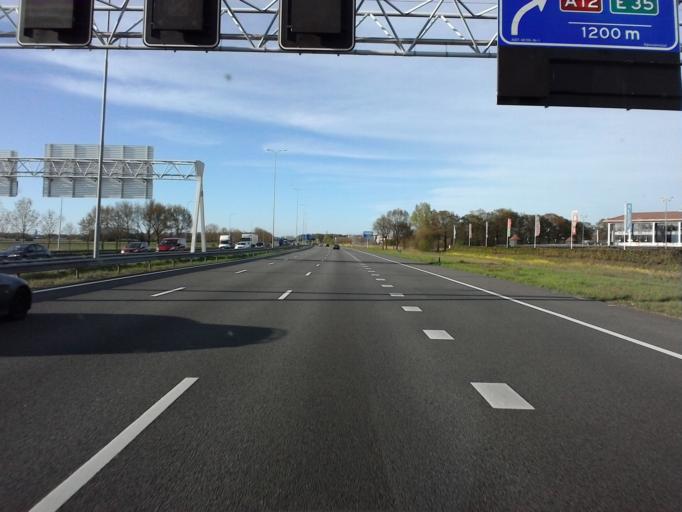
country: NL
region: Utrecht
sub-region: Gemeente Utrecht
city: Lunetten
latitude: 52.0346
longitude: 5.1378
